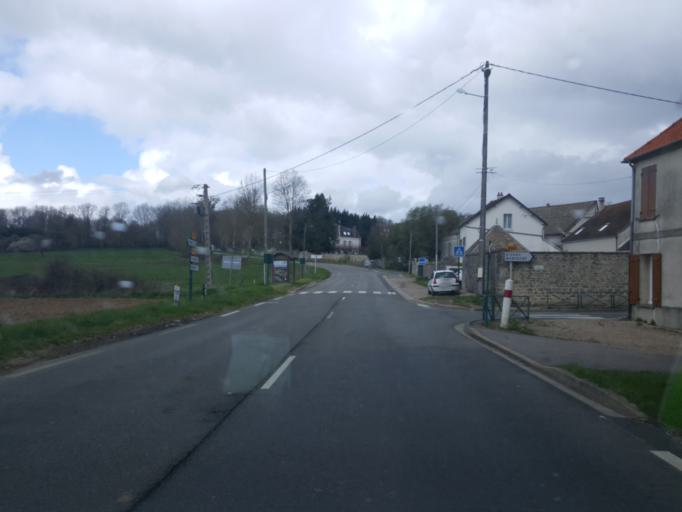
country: FR
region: Ile-de-France
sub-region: Departement du Val-d'Oise
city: Magny-en-Vexin
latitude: 49.1632
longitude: 1.7805
